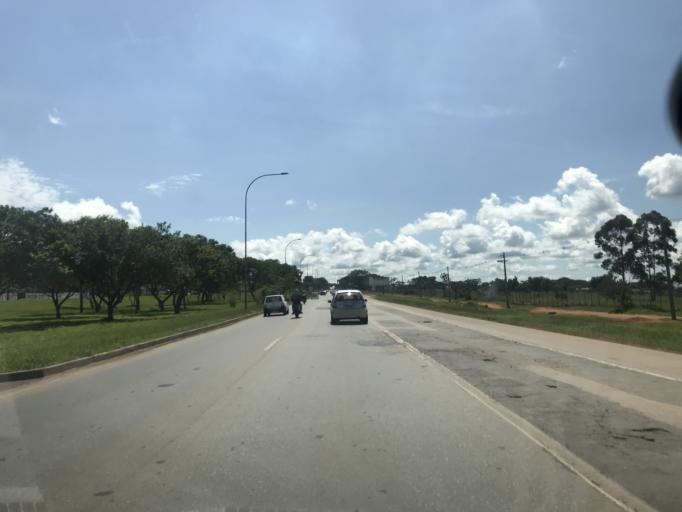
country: BR
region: Federal District
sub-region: Brasilia
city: Brasilia
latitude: -15.8751
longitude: -48.0353
